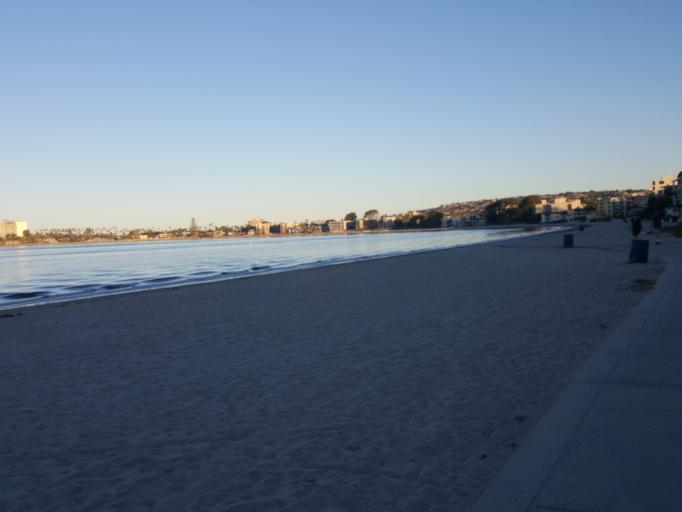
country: US
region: California
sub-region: San Diego County
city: La Jolla
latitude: 32.7856
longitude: -117.2399
